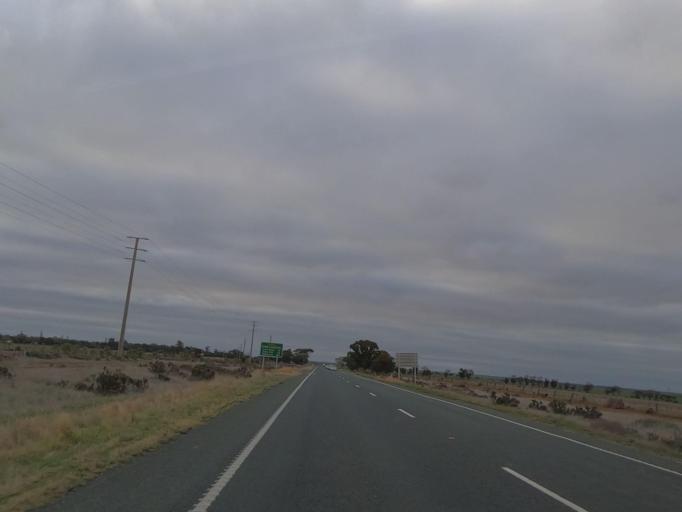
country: AU
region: Victoria
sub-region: Swan Hill
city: Swan Hill
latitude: -35.5678
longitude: 143.7847
